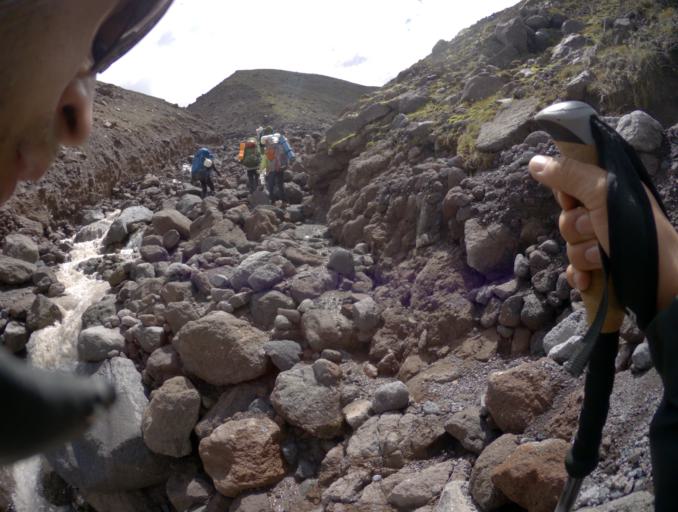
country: RU
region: Kabardino-Balkariya
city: Terskol
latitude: 43.3839
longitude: 42.3681
